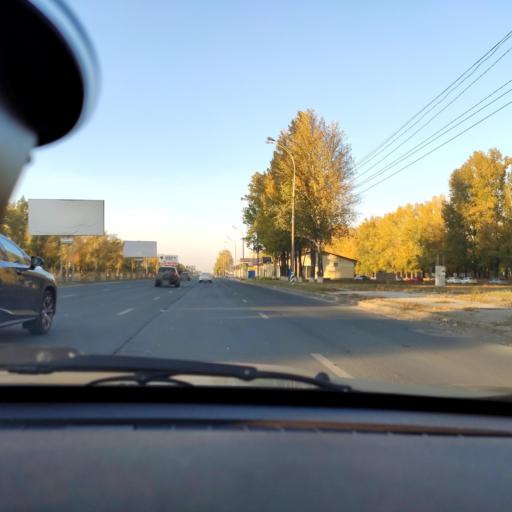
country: RU
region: Samara
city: Tol'yatti
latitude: 53.5209
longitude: 49.2799
